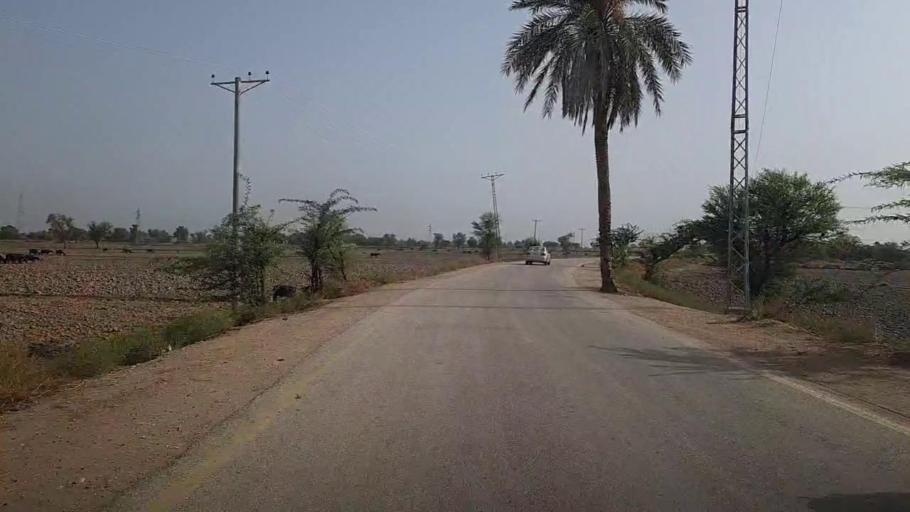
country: PK
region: Sindh
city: Khairpur Nathan Shah
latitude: 27.0997
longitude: 67.7554
